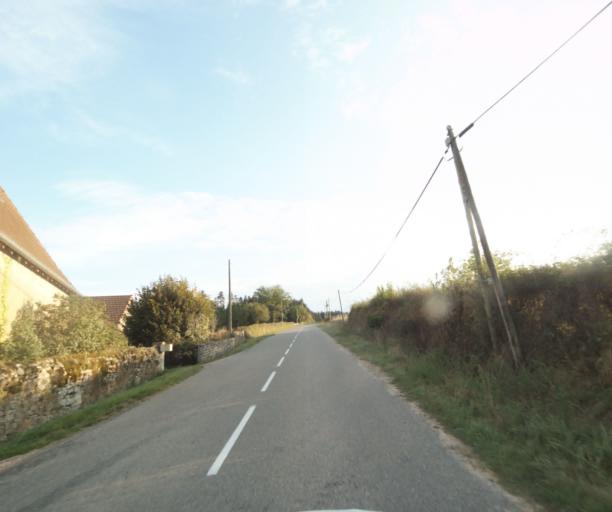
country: FR
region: Bourgogne
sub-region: Departement de Saone-et-Loire
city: Charolles
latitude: 46.4223
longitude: 4.4042
